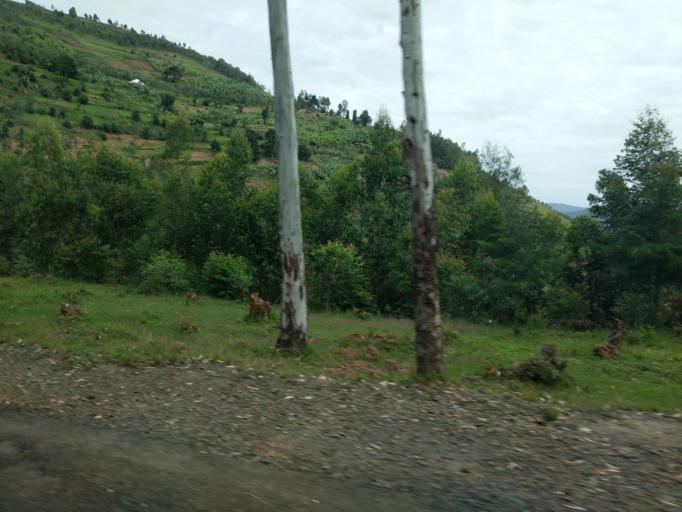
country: RW
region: Kigali
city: Kigali
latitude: -1.7869
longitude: 29.9279
